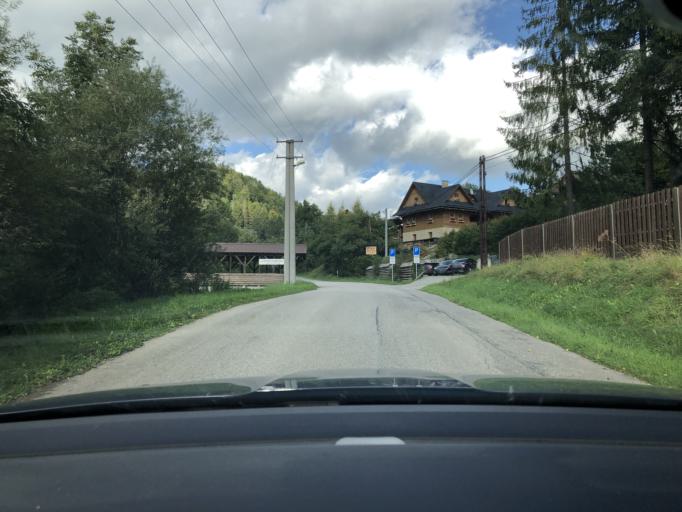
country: SK
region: Zilinsky
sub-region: Okres Zilina
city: Terchova
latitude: 49.2821
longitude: 19.0531
